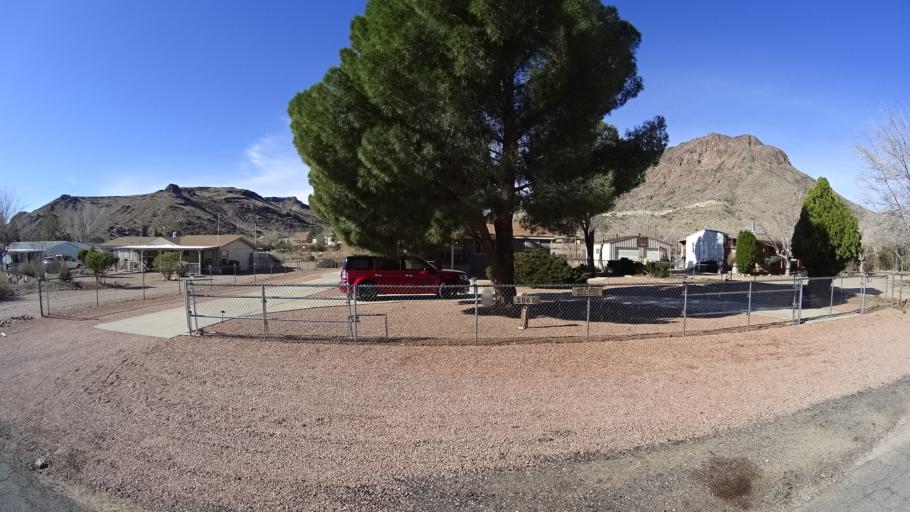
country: US
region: Arizona
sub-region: Mohave County
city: New Kingman-Butler
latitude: 35.2719
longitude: -114.0489
